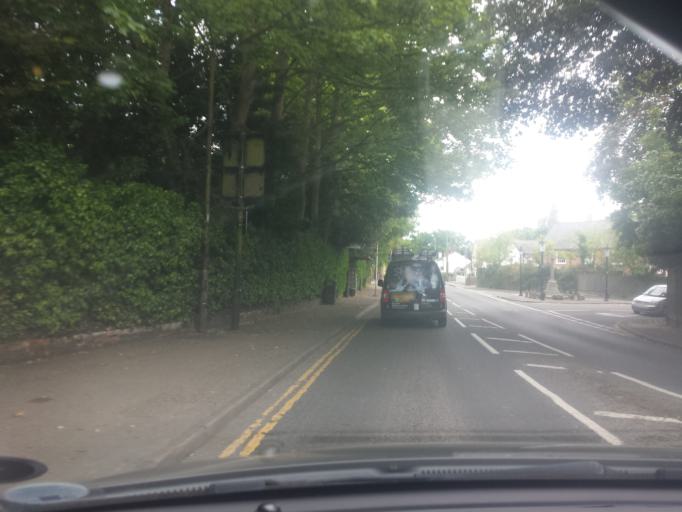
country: GB
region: England
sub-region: Essex
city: Little Clacton
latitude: 51.8563
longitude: 1.1653
